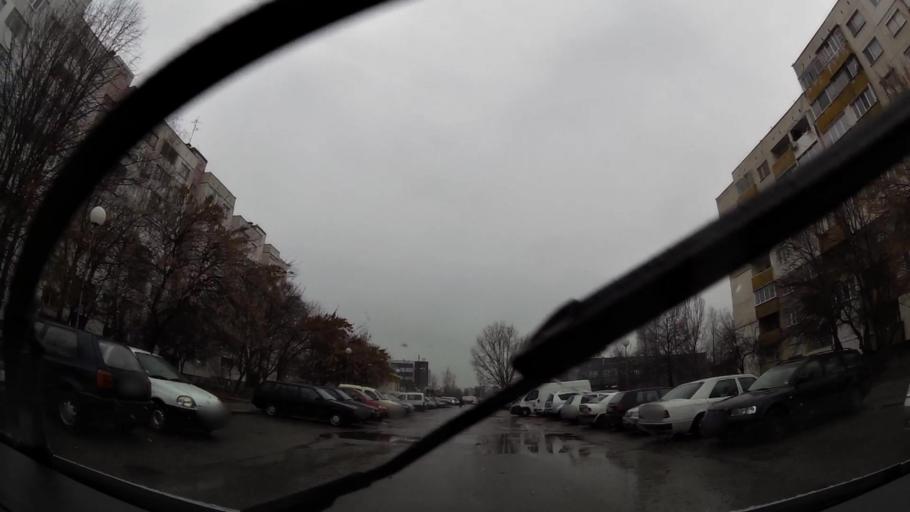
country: BG
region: Sofia-Capital
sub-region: Stolichna Obshtina
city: Sofia
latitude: 42.6432
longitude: 23.4091
